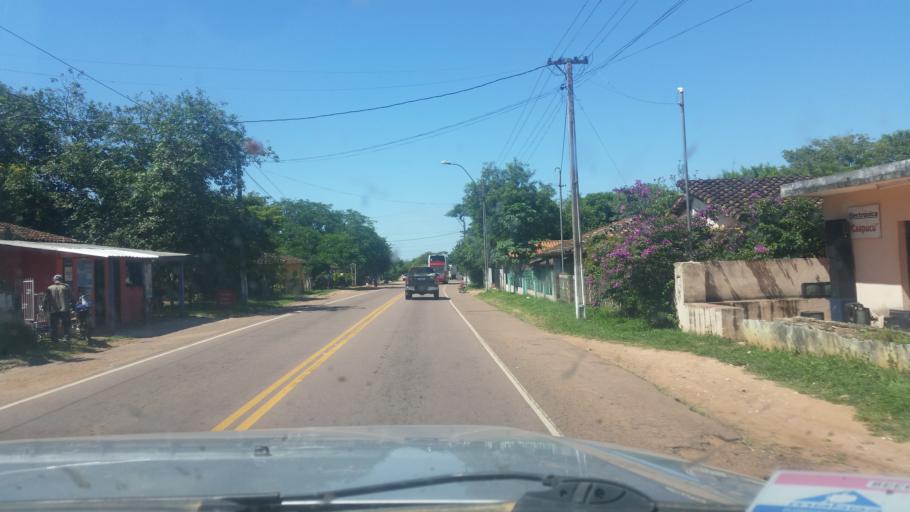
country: PY
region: Paraguari
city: Caapucu
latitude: -26.2350
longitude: -57.1782
